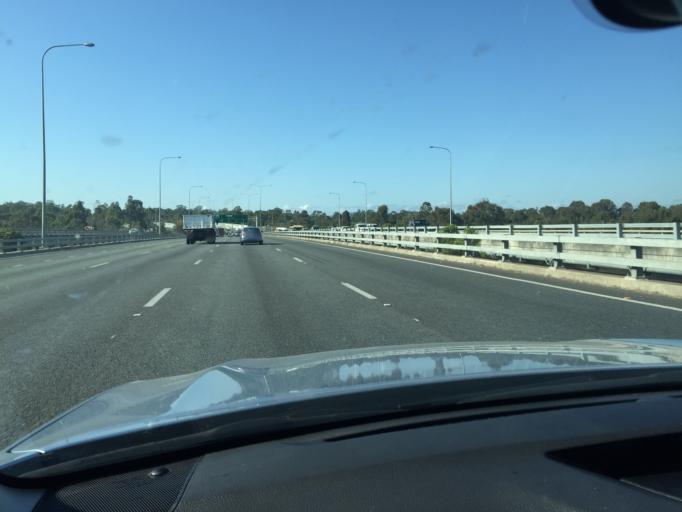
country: AU
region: Queensland
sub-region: Logan
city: Beenleigh
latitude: -27.6960
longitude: 153.1952
